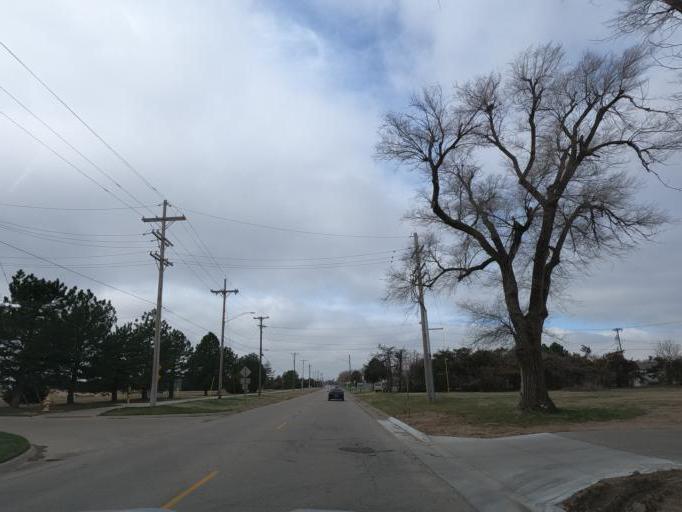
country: US
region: Kansas
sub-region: Reno County
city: Hutchinson
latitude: 38.0794
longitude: -97.9144
